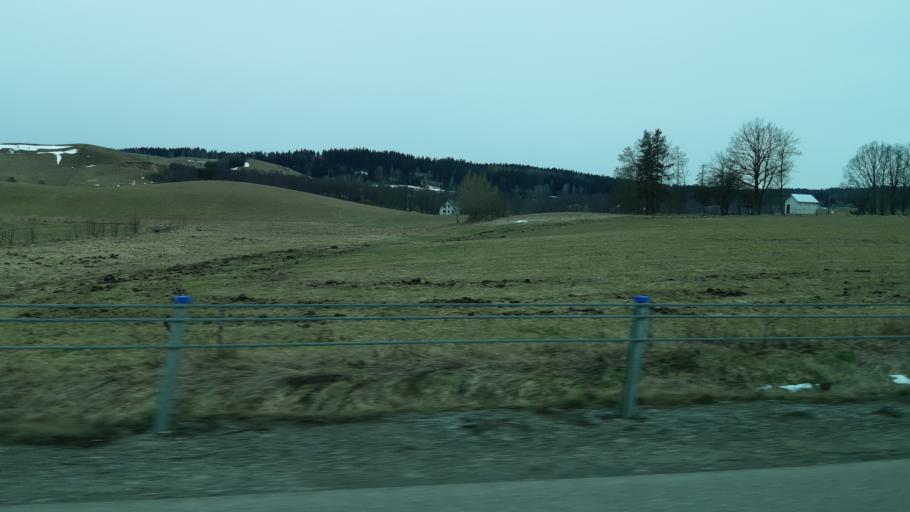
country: PL
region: Podlasie
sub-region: Suwalki
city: Suwalki
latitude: 54.3353
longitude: 22.9298
